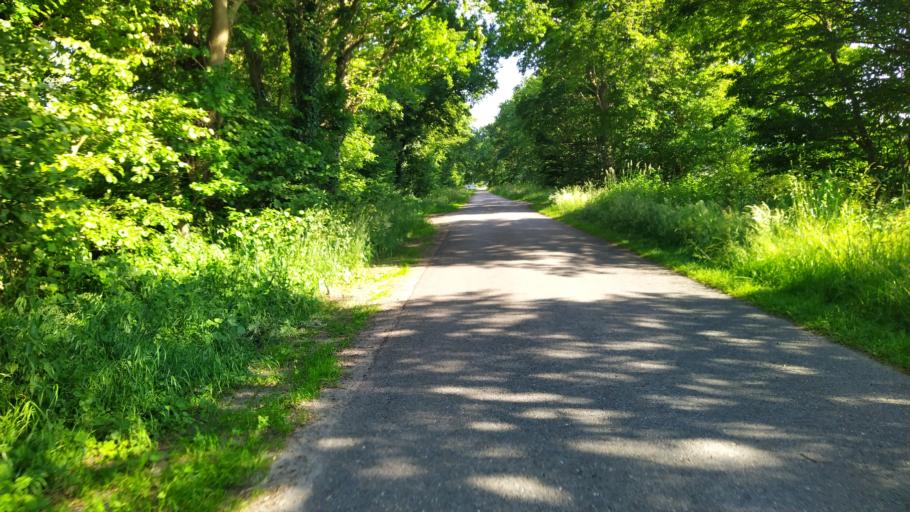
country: DE
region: Lower Saxony
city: Lintig
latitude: 53.6087
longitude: 8.8905
